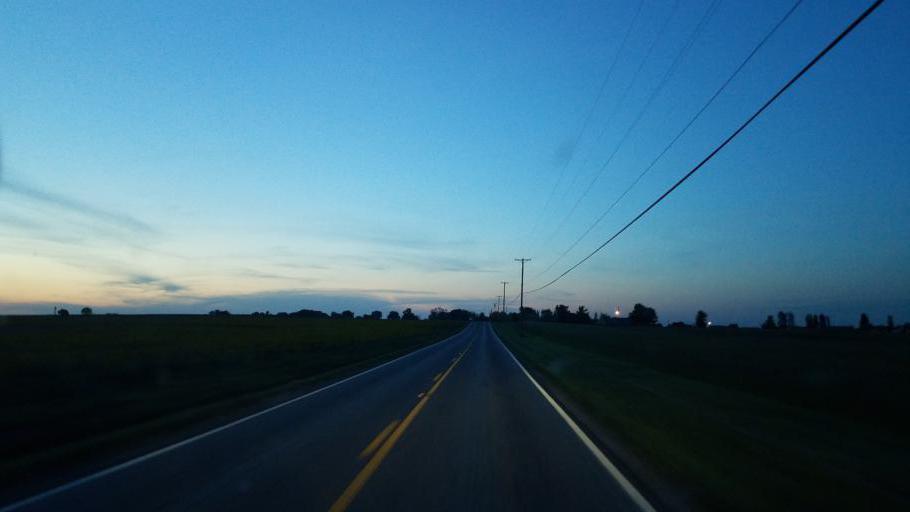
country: US
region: Ohio
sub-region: Highland County
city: Greenfield
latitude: 39.2531
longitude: -83.4410
